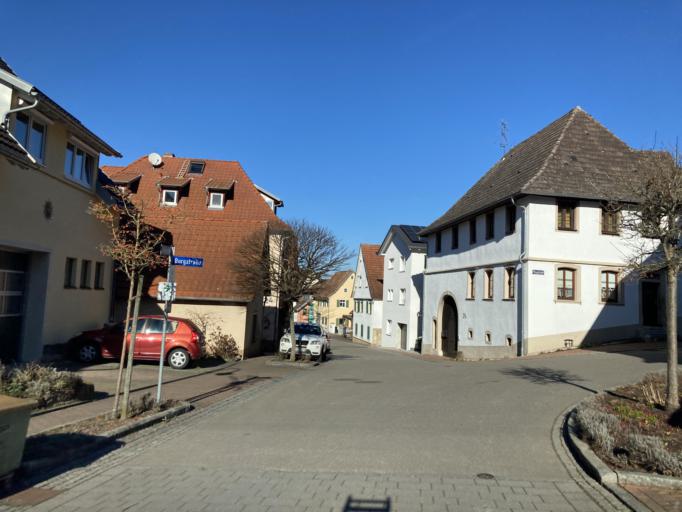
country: DE
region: Baden-Wuerttemberg
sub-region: Freiburg Region
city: Eichstetten
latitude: 48.1039
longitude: 7.7761
